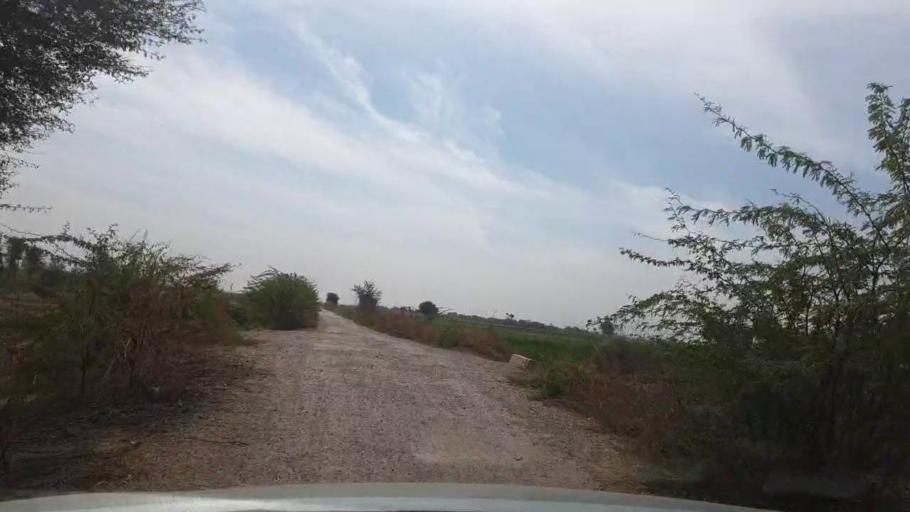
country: PK
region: Sindh
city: Nabisar
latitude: 25.1014
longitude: 69.6010
